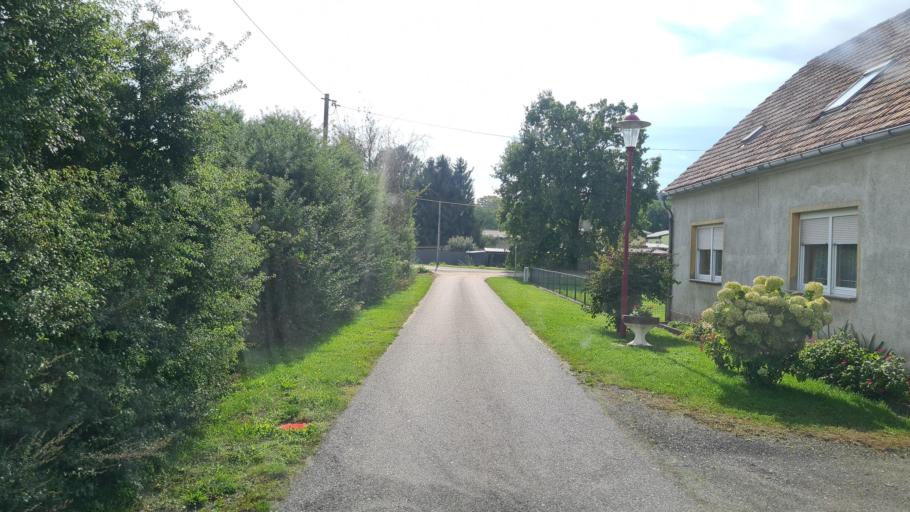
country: DE
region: Brandenburg
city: Sonnewalde
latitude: 51.7140
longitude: 13.6273
